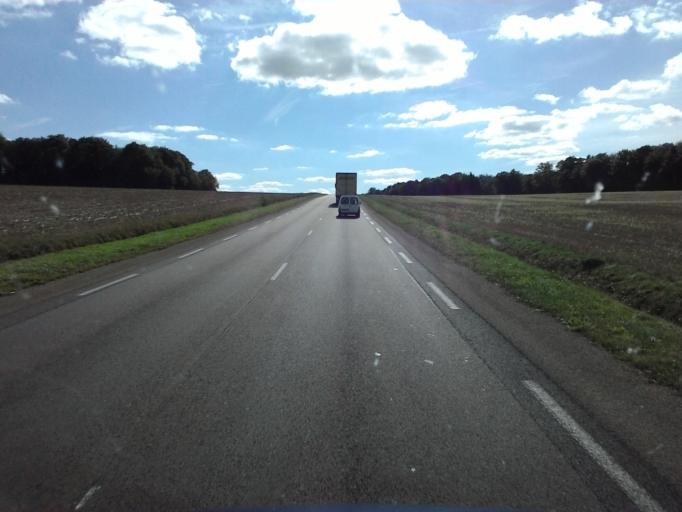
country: FR
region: Bourgogne
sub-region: Departement de la Cote-d'Or
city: Chatillon-sur-Seine
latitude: 47.7887
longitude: 4.5139
